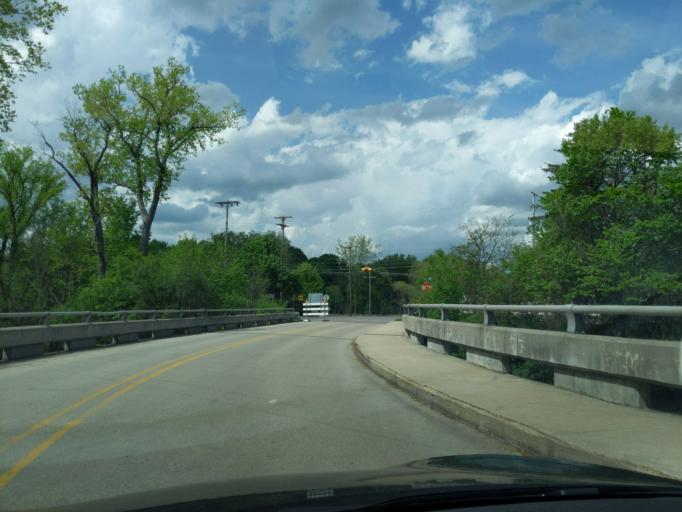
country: US
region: Michigan
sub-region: Ingham County
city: Okemos
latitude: 42.7227
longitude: -84.4374
